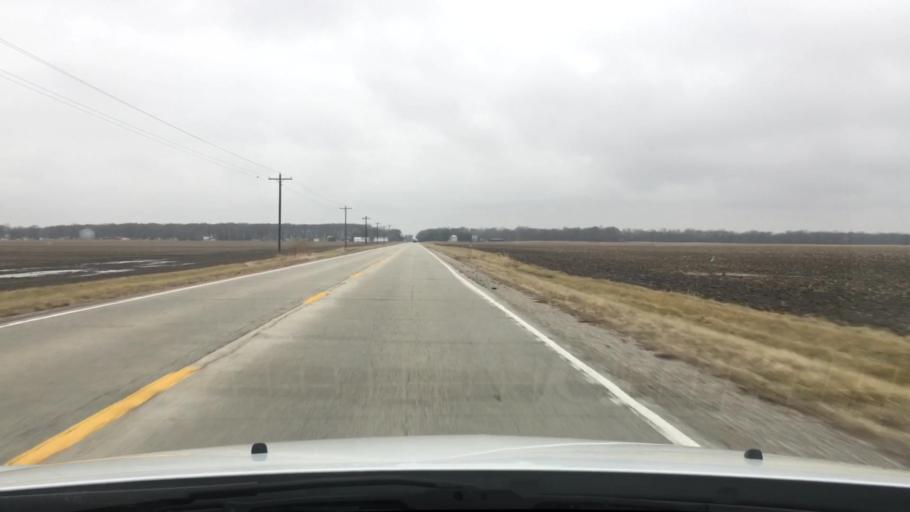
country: US
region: Illinois
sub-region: Iroquois County
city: Clifton
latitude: 40.8881
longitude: -87.8166
